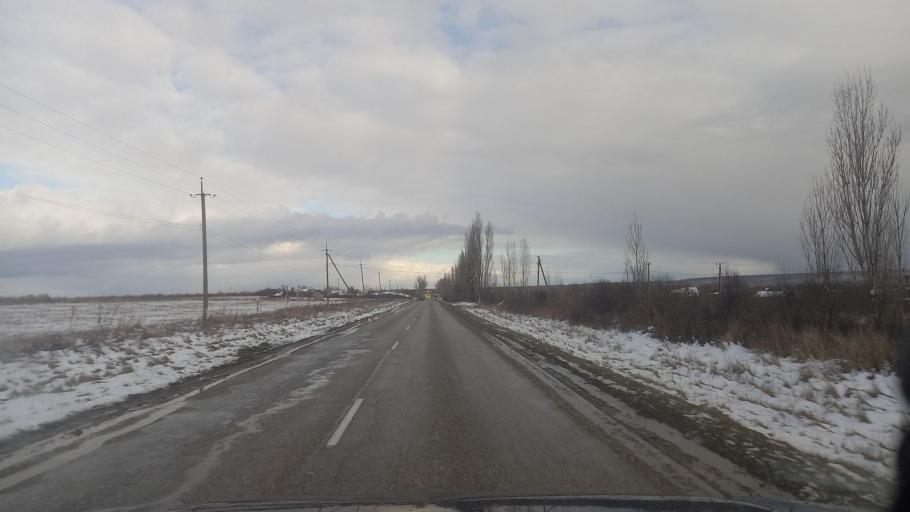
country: RU
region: Krasnodarskiy
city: Smolenskaya
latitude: 44.7738
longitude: 38.8256
